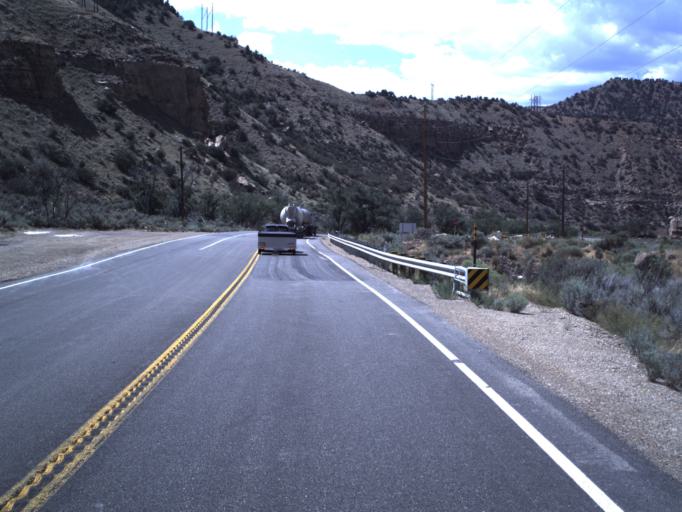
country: US
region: Utah
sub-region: Carbon County
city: Helper
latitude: 39.7297
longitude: -110.8544
